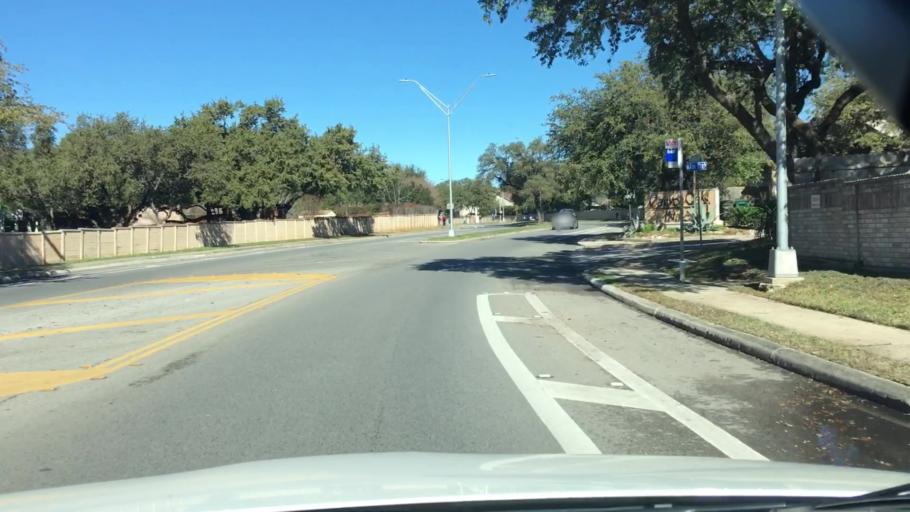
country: US
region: Texas
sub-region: Bexar County
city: Hollywood Park
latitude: 29.5995
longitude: -98.4571
